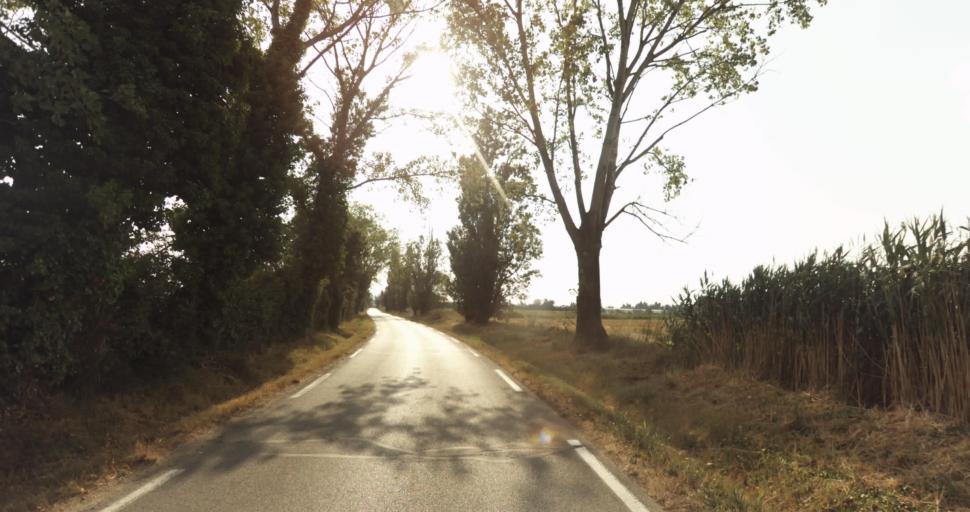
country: FR
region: Languedoc-Roussillon
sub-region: Departement des Pyrenees-Orientales
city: Corneilla-del-Vercol
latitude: 42.6215
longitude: 2.9634
